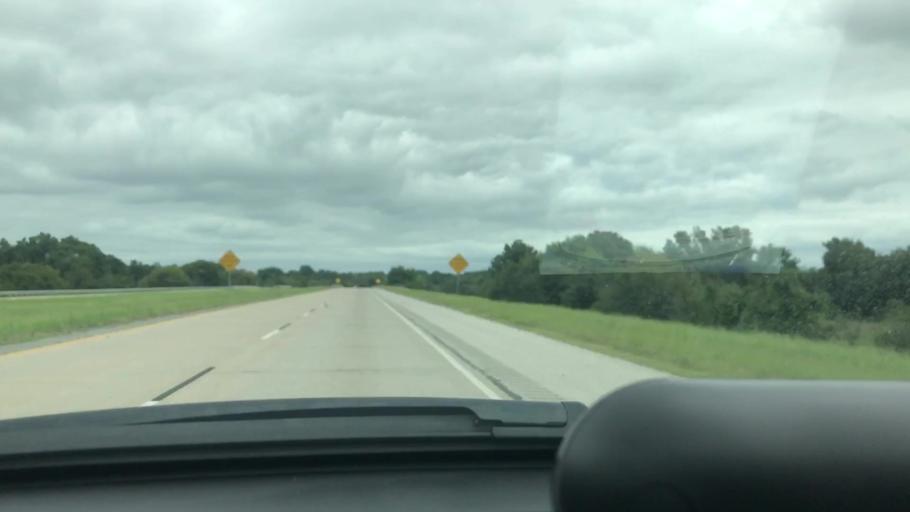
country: US
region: Oklahoma
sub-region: Wagoner County
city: Wagoner
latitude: 35.9058
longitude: -95.4026
